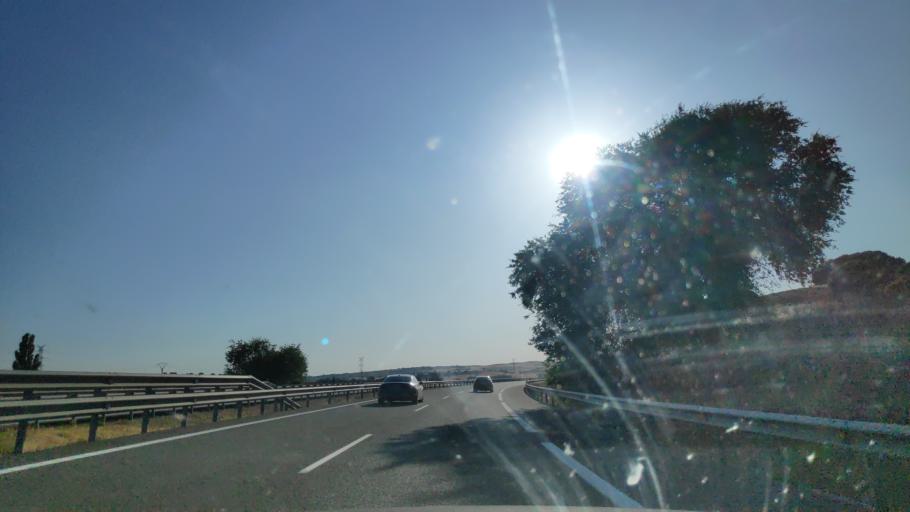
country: ES
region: Castille-La Mancha
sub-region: Provincia de Cuenca
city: Zafra de Zancara
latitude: 39.8593
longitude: -2.5504
